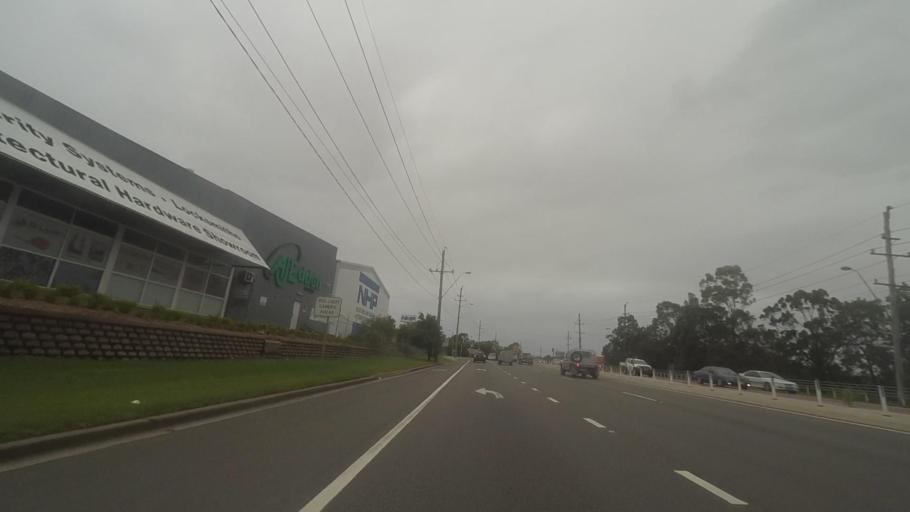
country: AU
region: New South Wales
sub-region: Newcastle
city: Mayfield West
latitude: -32.8810
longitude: 151.7183
